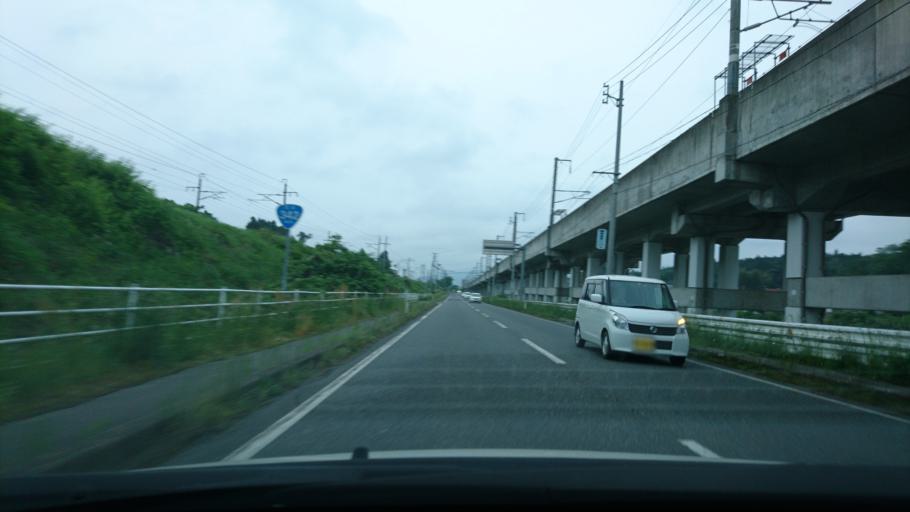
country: JP
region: Iwate
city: Ichinoseki
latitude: 38.9011
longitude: 141.1294
